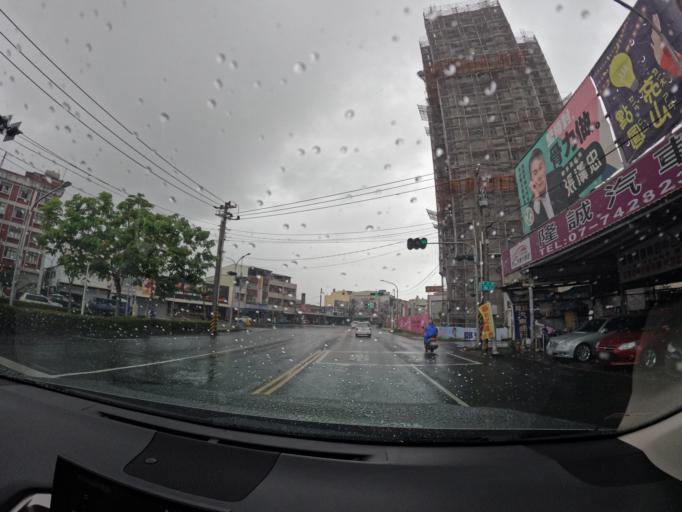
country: TW
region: Taiwan
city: Fengshan
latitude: 22.6411
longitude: 120.3642
